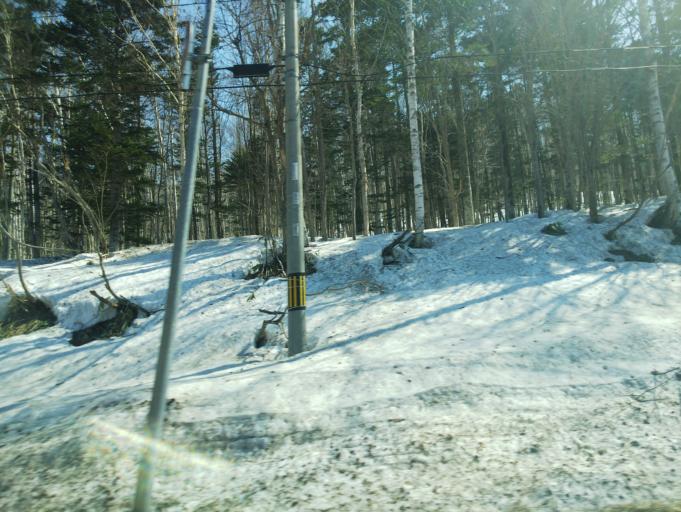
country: JP
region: Hokkaido
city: Nayoro
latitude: 44.7149
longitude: 142.2729
